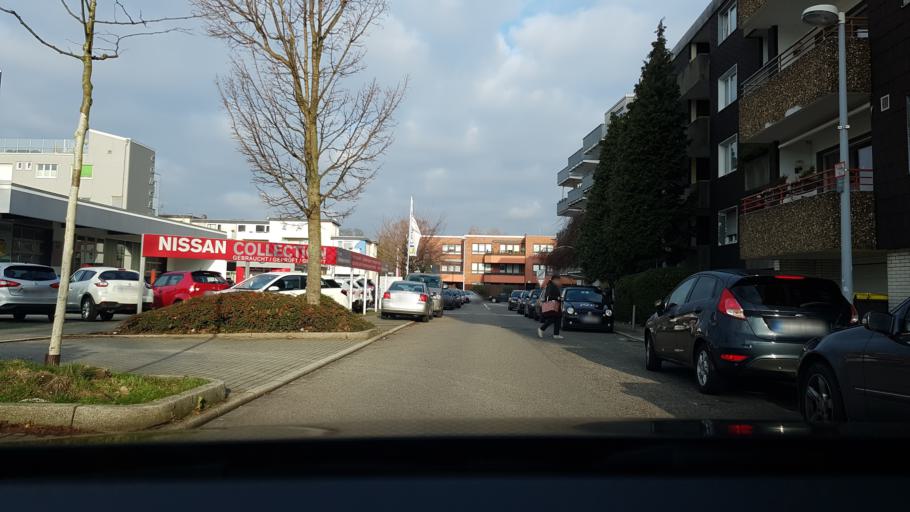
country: DE
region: North Rhine-Westphalia
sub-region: Regierungsbezirk Dusseldorf
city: Muelheim (Ruhr)
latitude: 51.4344
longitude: 6.9215
